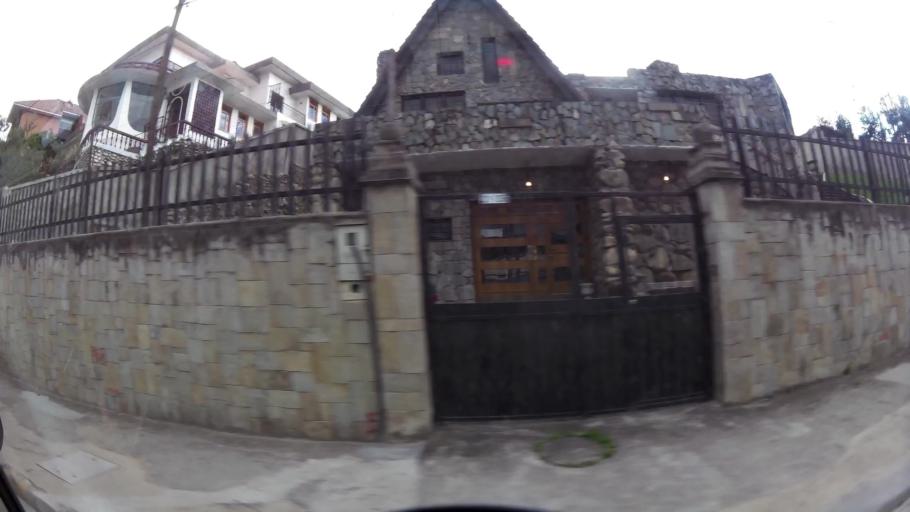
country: EC
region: Azuay
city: Cuenca
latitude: -2.8922
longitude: -79.0173
